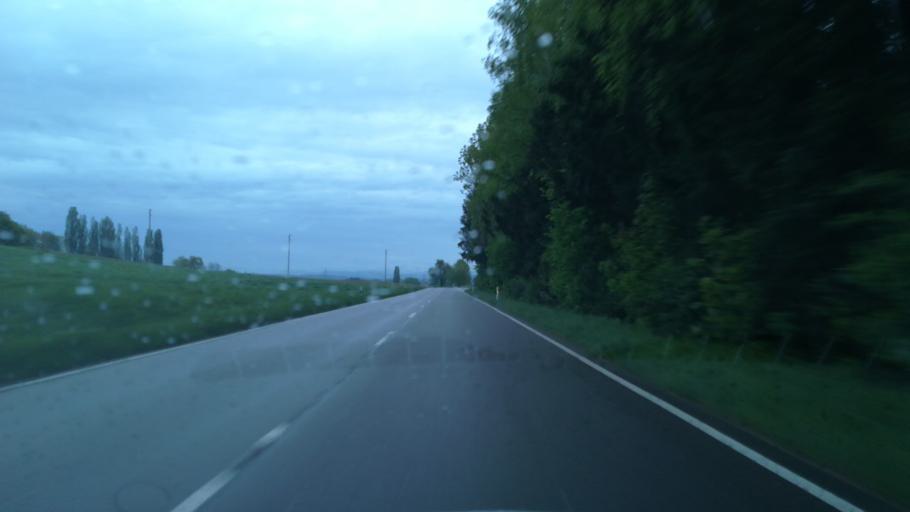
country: DE
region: Baden-Wuerttemberg
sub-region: Freiburg Region
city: Lottstetten
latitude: 47.6388
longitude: 8.5722
